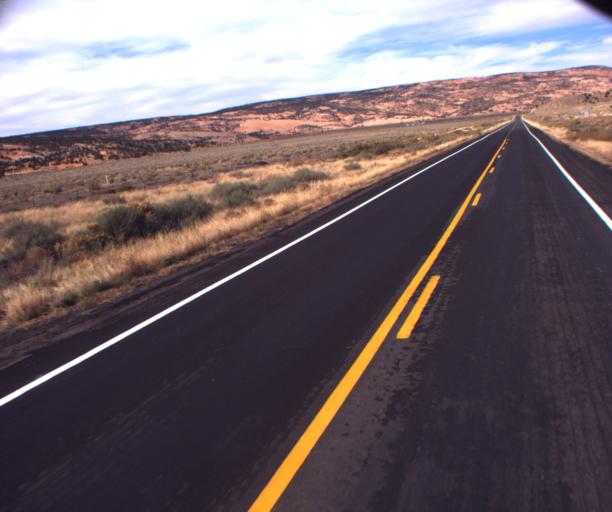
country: US
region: Arizona
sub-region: Navajo County
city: Kayenta
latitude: 36.5961
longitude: -110.4724
